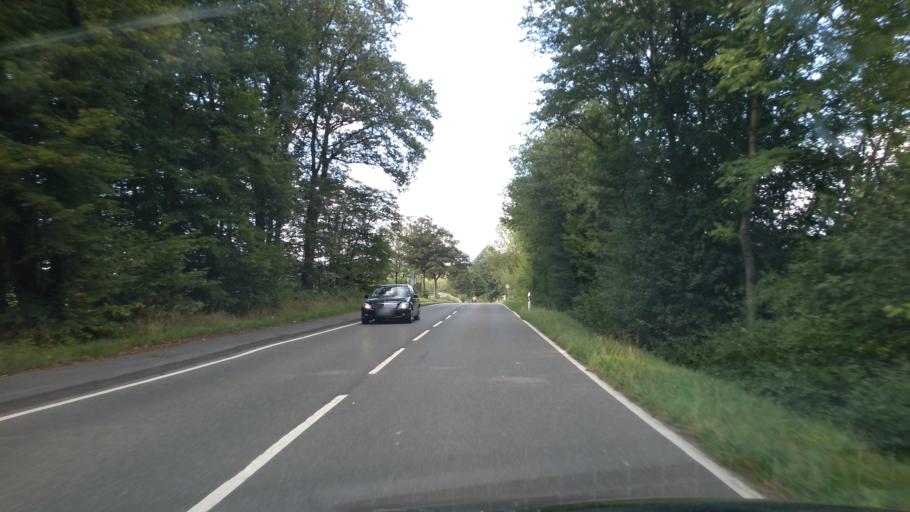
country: DE
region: North Rhine-Westphalia
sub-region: Regierungsbezirk Koln
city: Much
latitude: 50.8782
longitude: 7.3851
